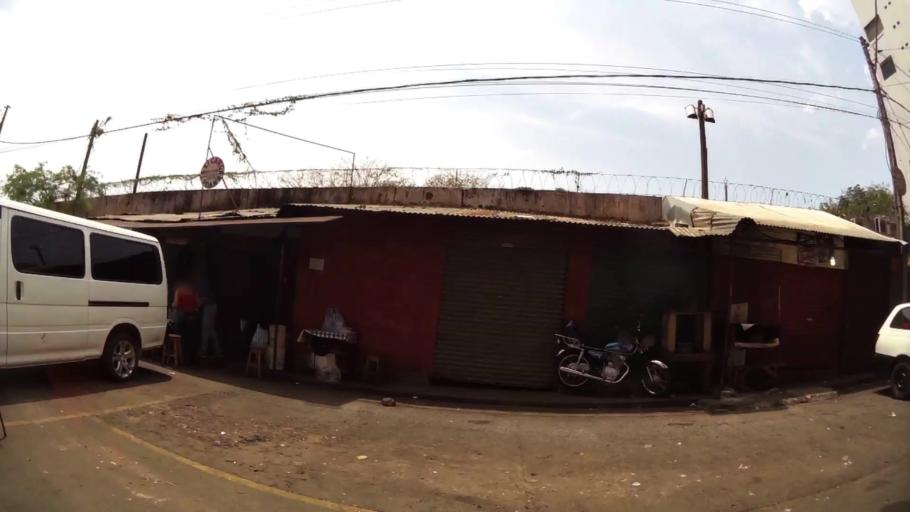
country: PY
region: Alto Parana
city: Ciudad del Este
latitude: -25.5080
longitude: -54.6076
